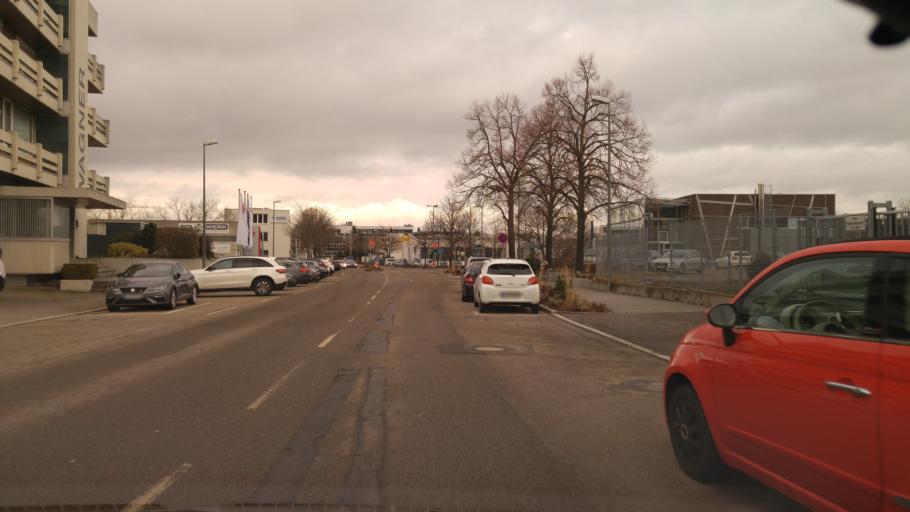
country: DE
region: Baden-Wuerttemberg
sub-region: Regierungsbezirk Stuttgart
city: Gerlingen
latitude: 48.8038
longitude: 9.0747
